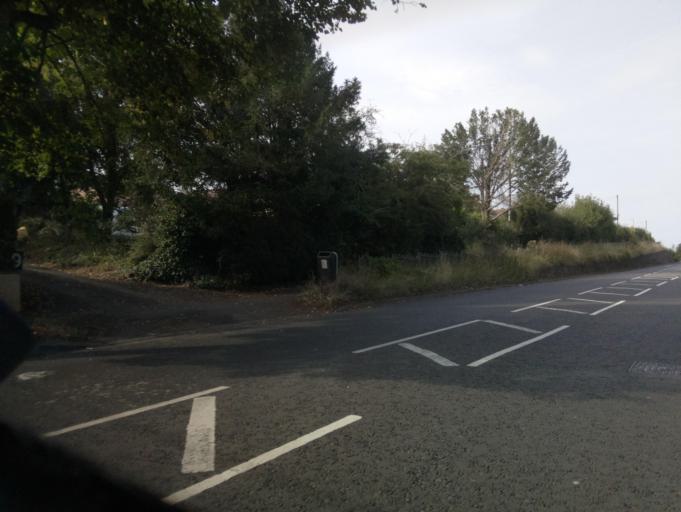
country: GB
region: England
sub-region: Worcestershire
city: Evesham
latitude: 52.1001
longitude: -1.9451
